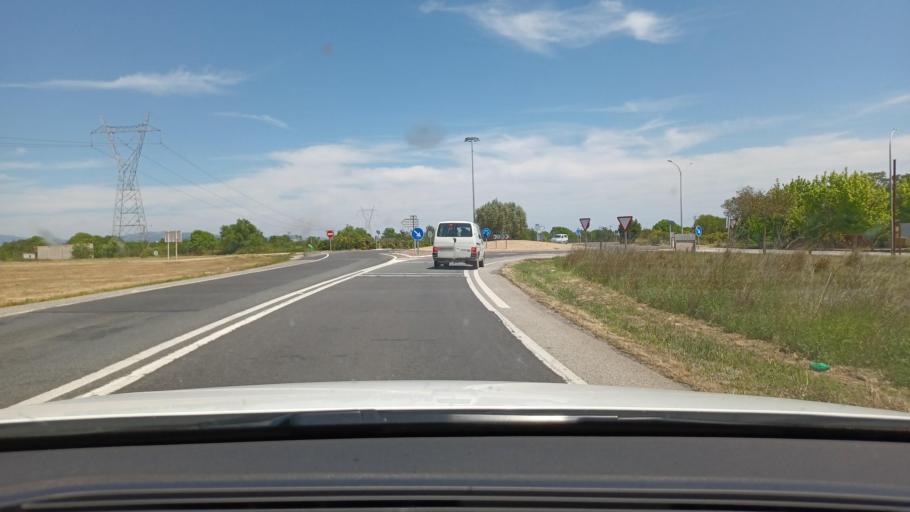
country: ES
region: Catalonia
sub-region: Provincia de Tarragona
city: Santa Barbara
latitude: 40.6853
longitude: 0.4634
